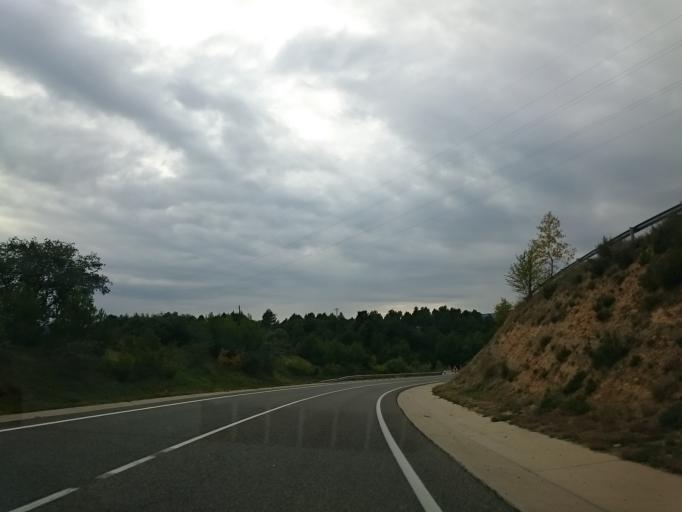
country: ES
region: Catalonia
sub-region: Provincia de Lleida
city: Tremp
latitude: 42.1844
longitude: 0.9166
